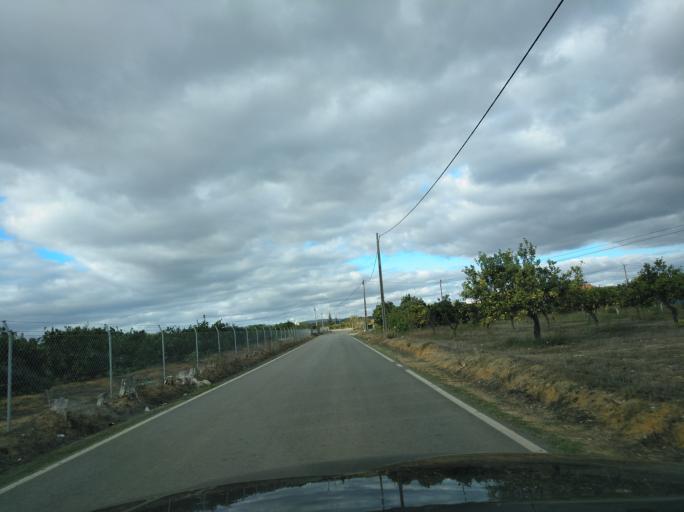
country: PT
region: Faro
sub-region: Tavira
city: Luz
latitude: 37.1031
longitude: -7.7088
